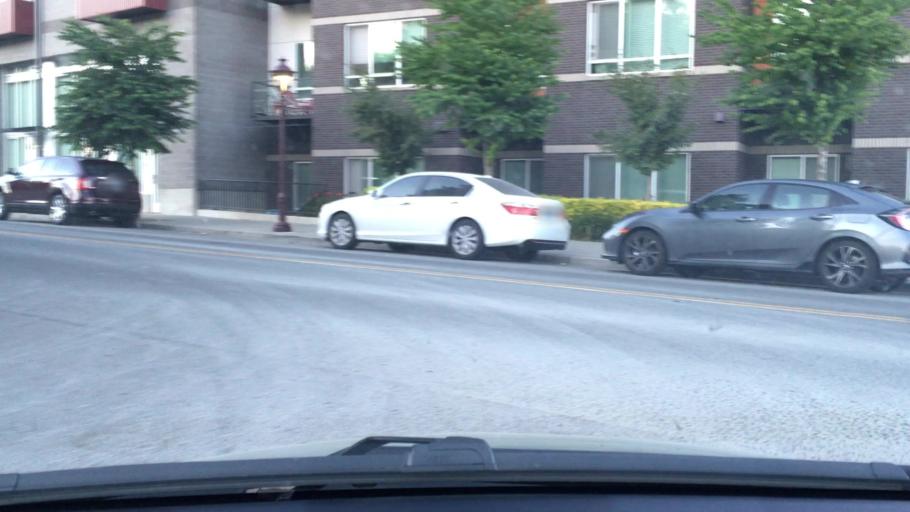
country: US
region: Washington
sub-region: King County
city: Inglewood-Finn Hill
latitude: 47.7058
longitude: -122.2131
